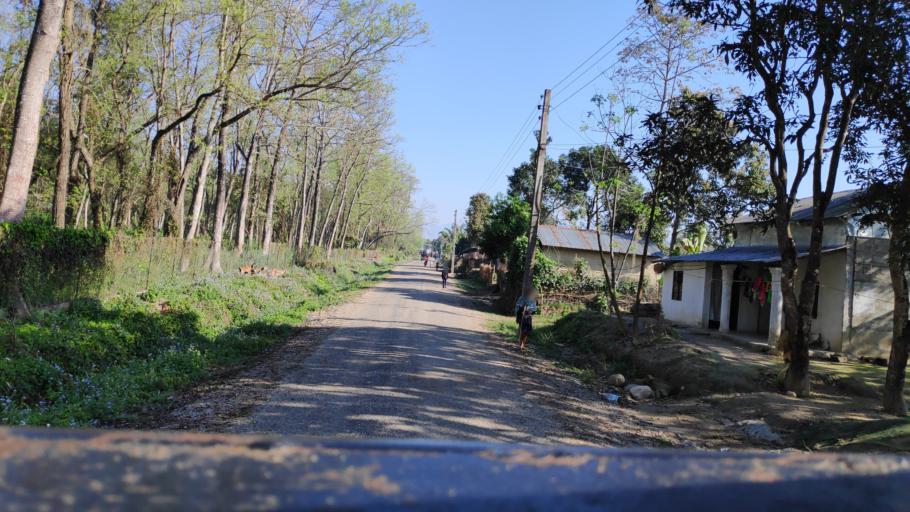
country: NP
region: Central Region
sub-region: Narayani Zone
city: Bharatpur
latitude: 27.5718
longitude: 84.5177
